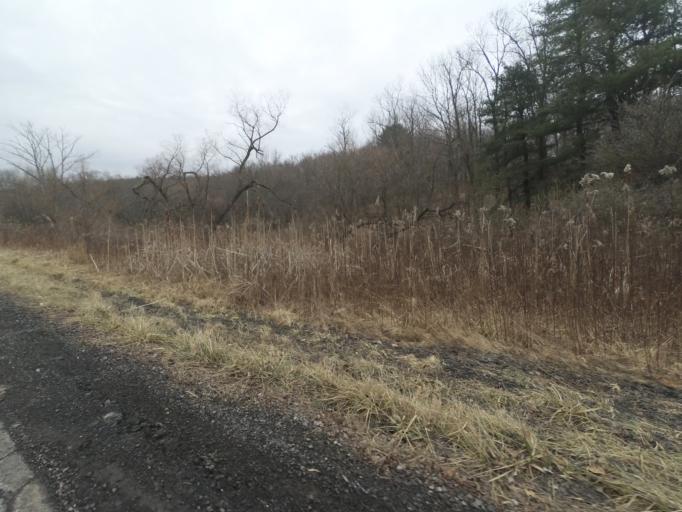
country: US
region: Pennsylvania
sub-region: Centre County
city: Stormstown
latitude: 40.8667
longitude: -78.0065
